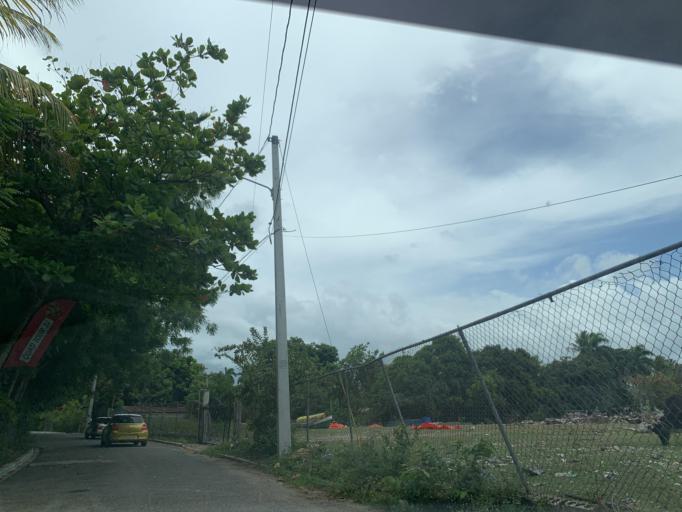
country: DO
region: Puerto Plata
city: Imbert
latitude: 19.8258
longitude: -70.7786
